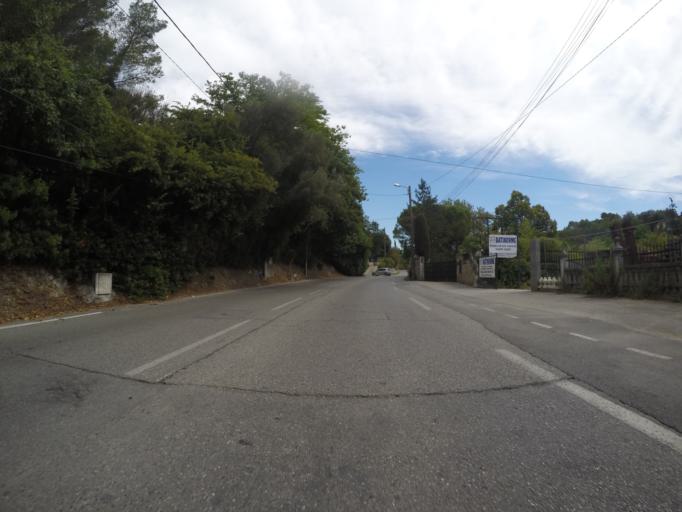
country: FR
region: Provence-Alpes-Cote d'Azur
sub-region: Departement des Alpes-Maritimes
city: Mougins
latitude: 43.6054
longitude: 6.9923
